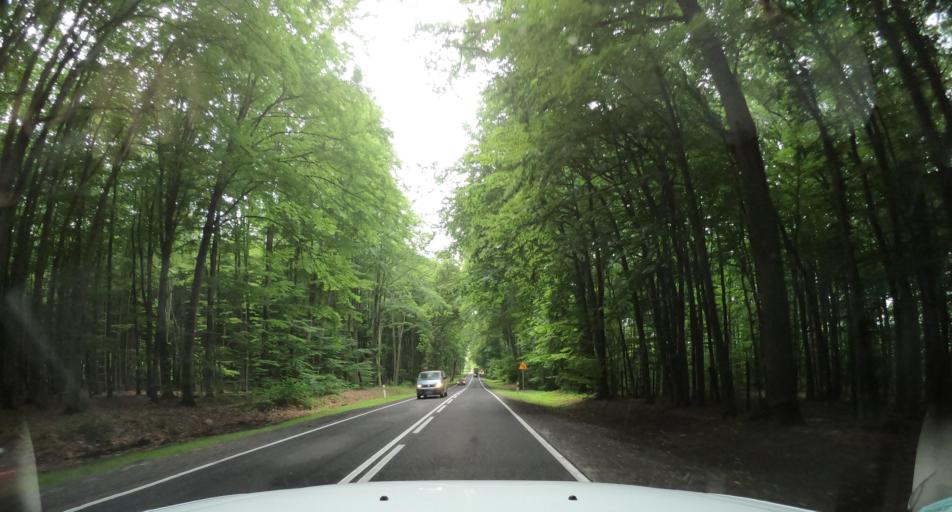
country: PL
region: West Pomeranian Voivodeship
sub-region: Powiat walecki
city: Walcz
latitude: 53.2568
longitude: 16.4225
